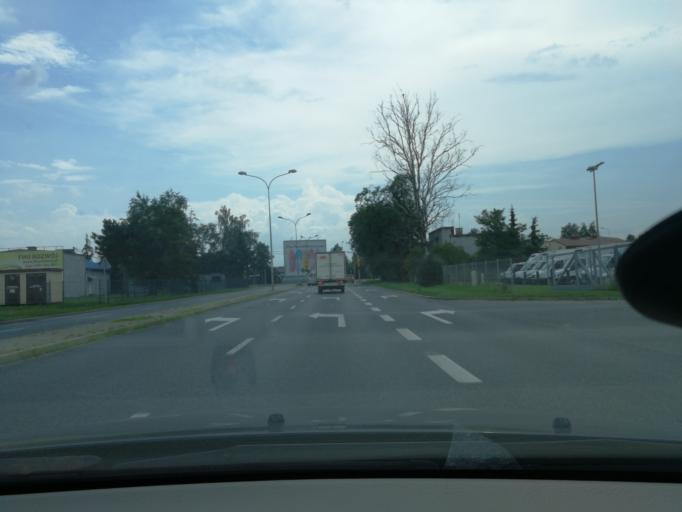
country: PL
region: Masovian Voivodeship
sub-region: Powiat pruszkowski
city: Piastow
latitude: 52.2156
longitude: 20.8388
